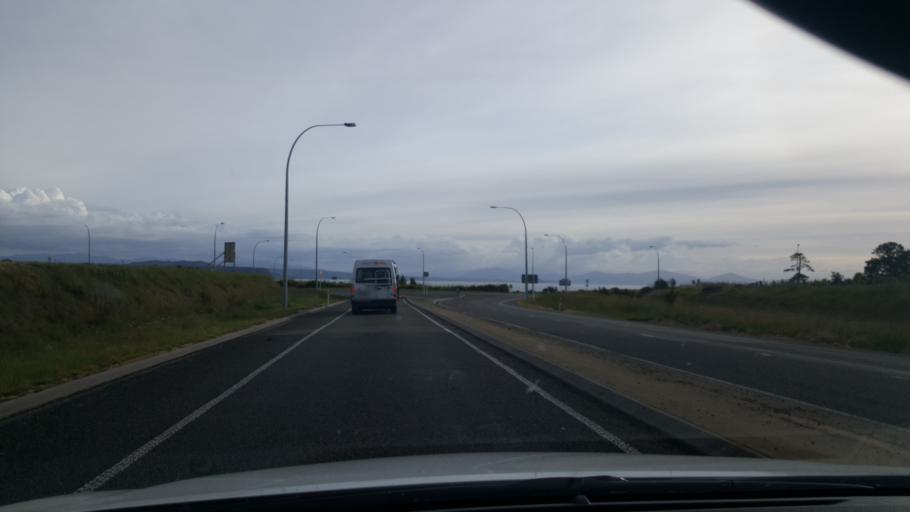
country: NZ
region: Waikato
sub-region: Taupo District
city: Taupo
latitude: -38.7378
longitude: 176.0735
